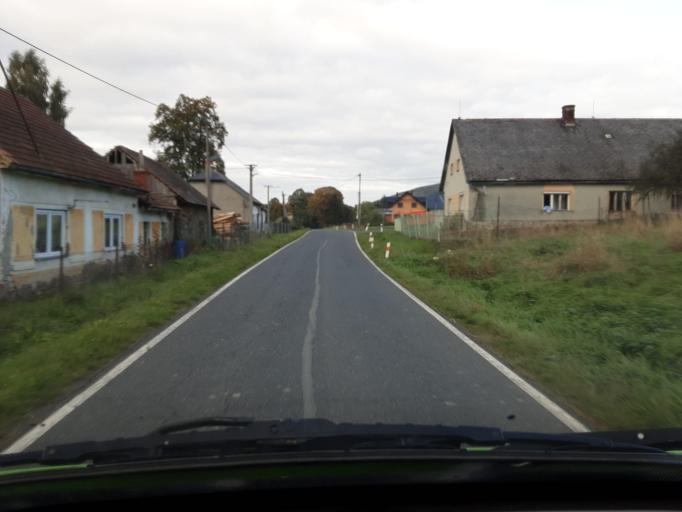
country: CZ
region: Plzensky
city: Janovice nad Uhlavou
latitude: 49.4125
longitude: 13.1628
